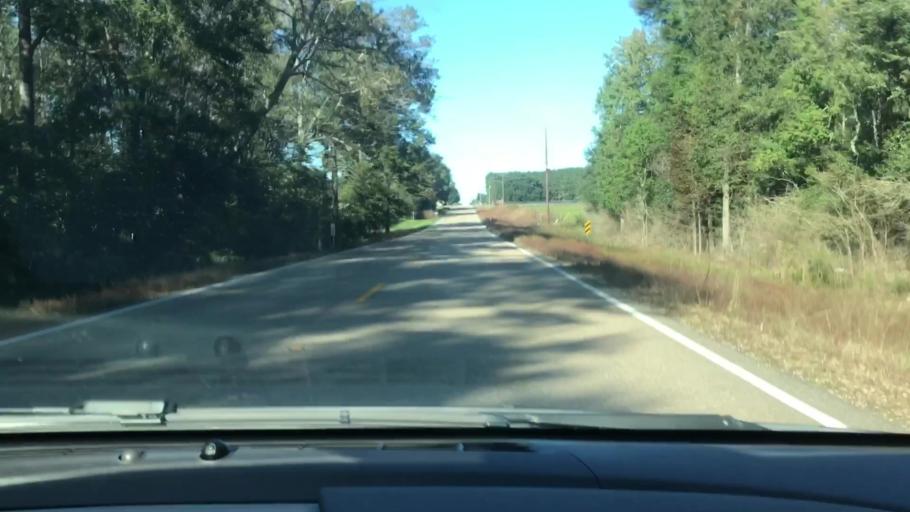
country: US
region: Louisiana
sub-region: Saint Tammany Parish
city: Abita Springs
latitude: 30.5773
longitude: -90.0366
